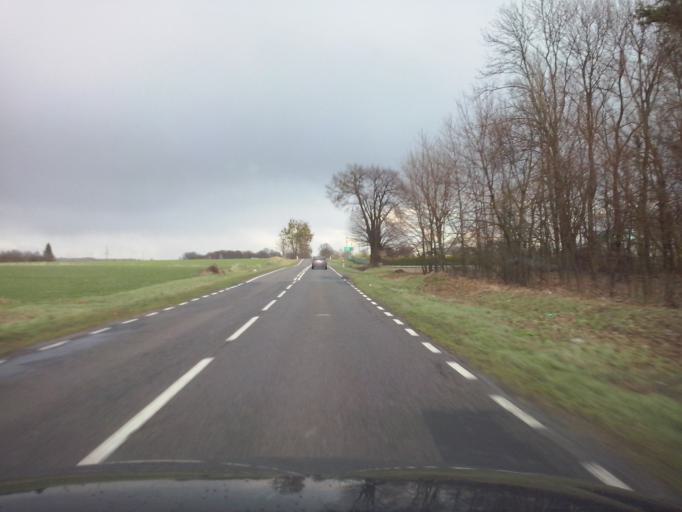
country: PL
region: Lublin Voivodeship
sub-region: Powiat krasnostawski
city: Krasnystaw
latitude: 51.0235
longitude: 23.2105
